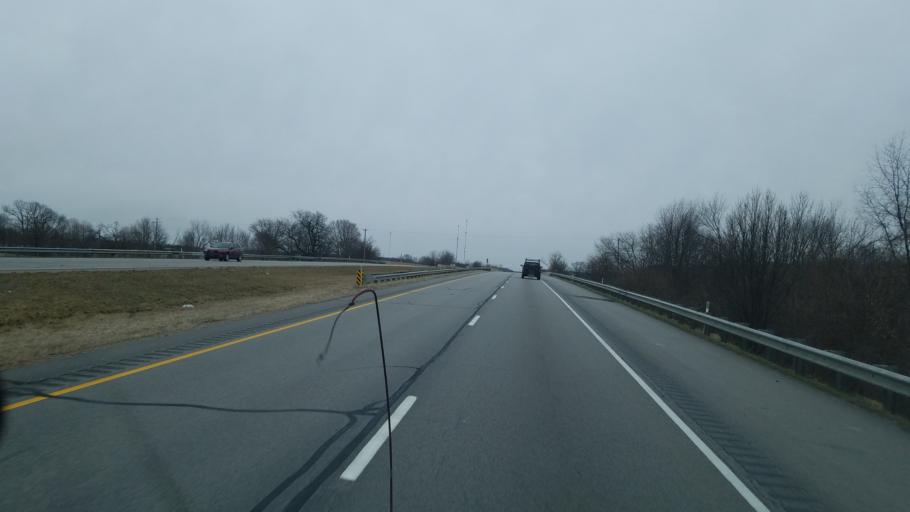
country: US
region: Indiana
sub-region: Marshall County
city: Plymouth
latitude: 41.3347
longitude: -86.2763
